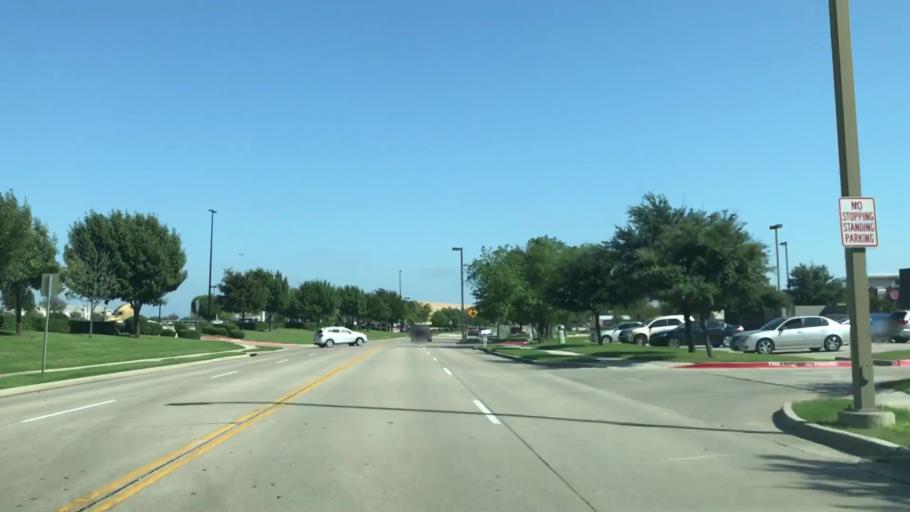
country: US
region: Texas
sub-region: Dallas County
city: Coppell
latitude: 32.9185
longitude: -96.9641
